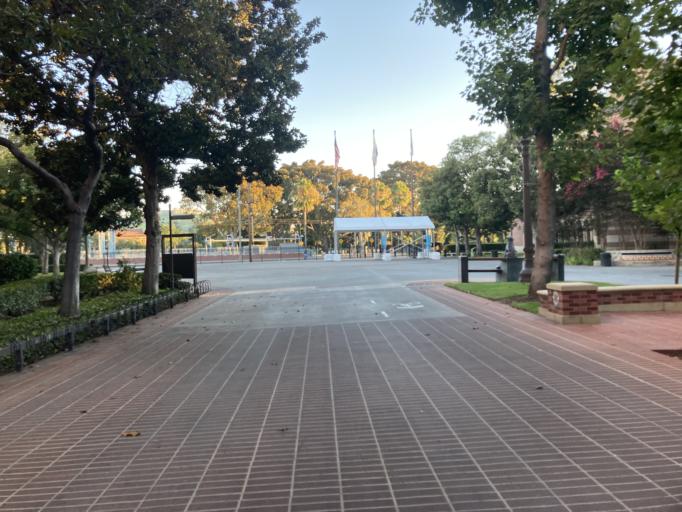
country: US
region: California
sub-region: Los Angeles County
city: Los Angeles
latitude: 34.0190
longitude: -118.2861
